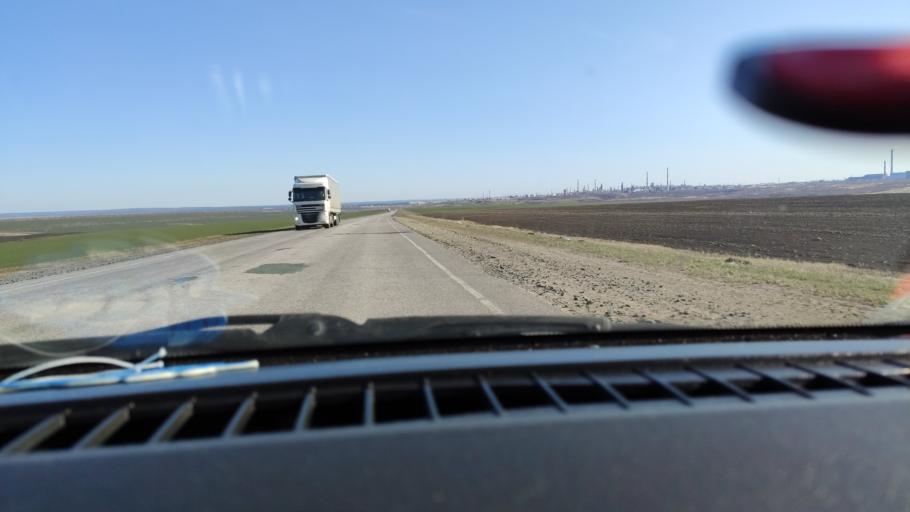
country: RU
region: Samara
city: Varlamovo
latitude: 53.0407
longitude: 48.3392
